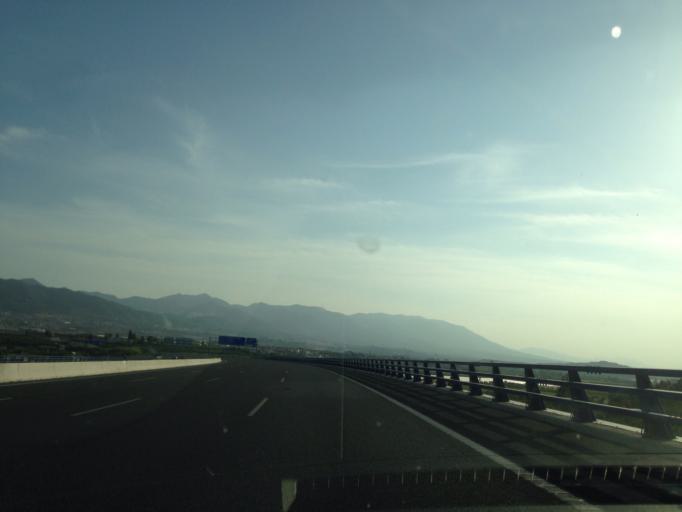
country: ES
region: Andalusia
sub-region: Provincia de Malaga
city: Alhaurin de la Torre
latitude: 36.6948
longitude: -4.5227
